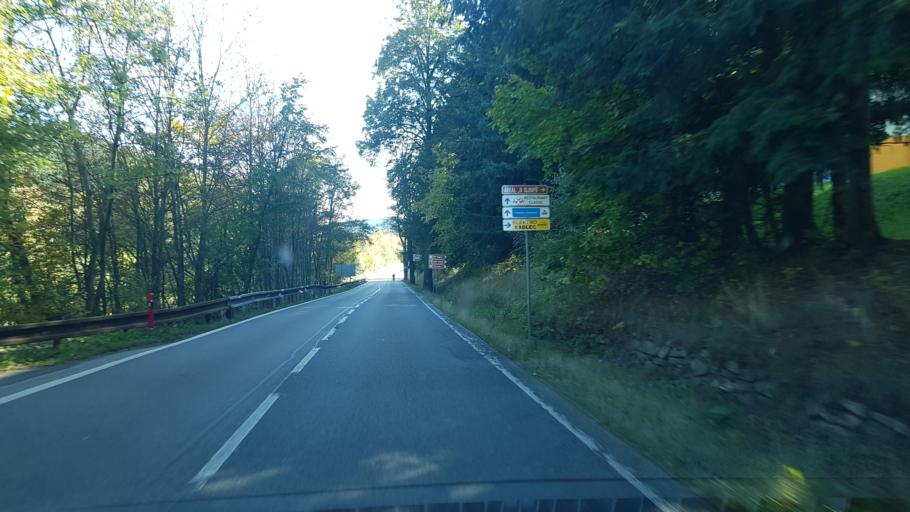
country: CZ
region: Jihocesky
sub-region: Okres Prachatice
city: Vimperk
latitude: 49.0625
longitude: 13.7826
